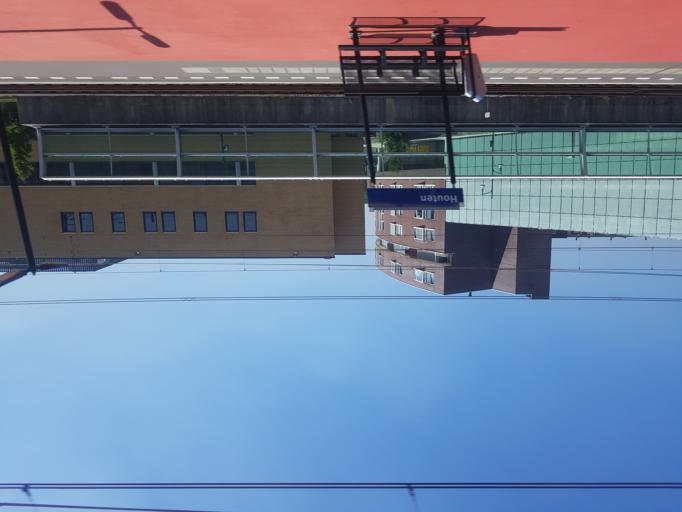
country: NL
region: Utrecht
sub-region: Gemeente Houten
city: Houten
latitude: 52.0330
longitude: 5.1689
